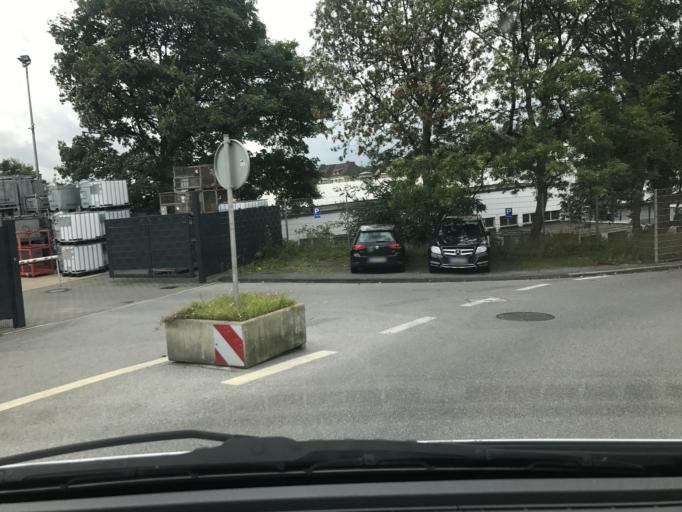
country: DE
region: North Rhine-Westphalia
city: Ennepetal
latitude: 51.3372
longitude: 7.3909
